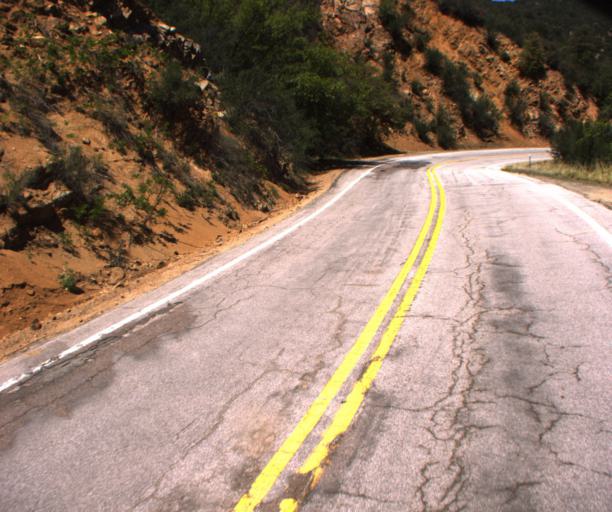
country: US
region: Arizona
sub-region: Yavapai County
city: Prescott
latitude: 34.4538
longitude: -112.5390
